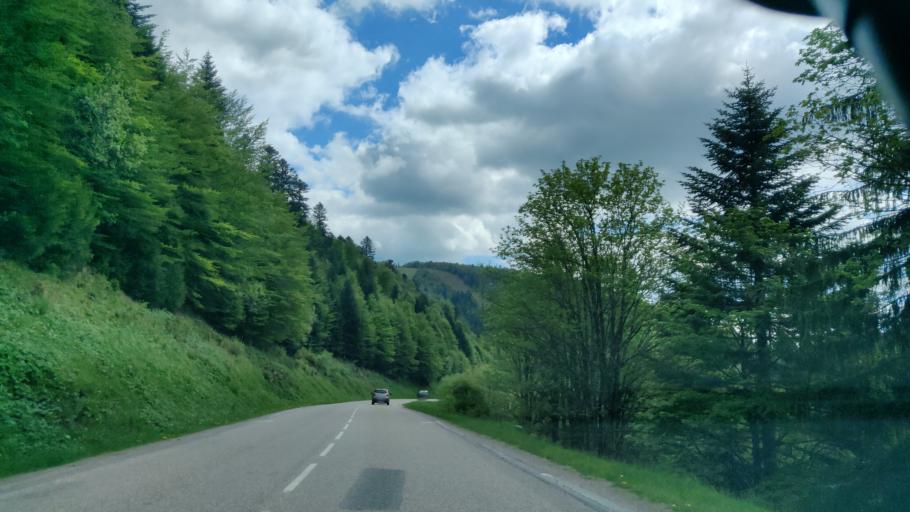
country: FR
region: Lorraine
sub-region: Departement des Vosges
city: Xonrupt-Longemer
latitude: 48.0444
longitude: 6.9761
